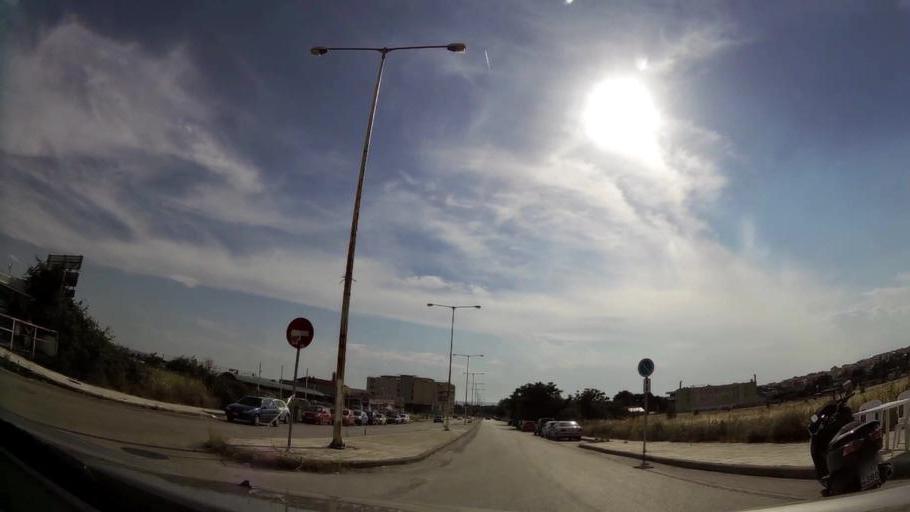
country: GR
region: Central Macedonia
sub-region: Nomos Thessalonikis
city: Pylaia
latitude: 40.5660
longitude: 22.9798
